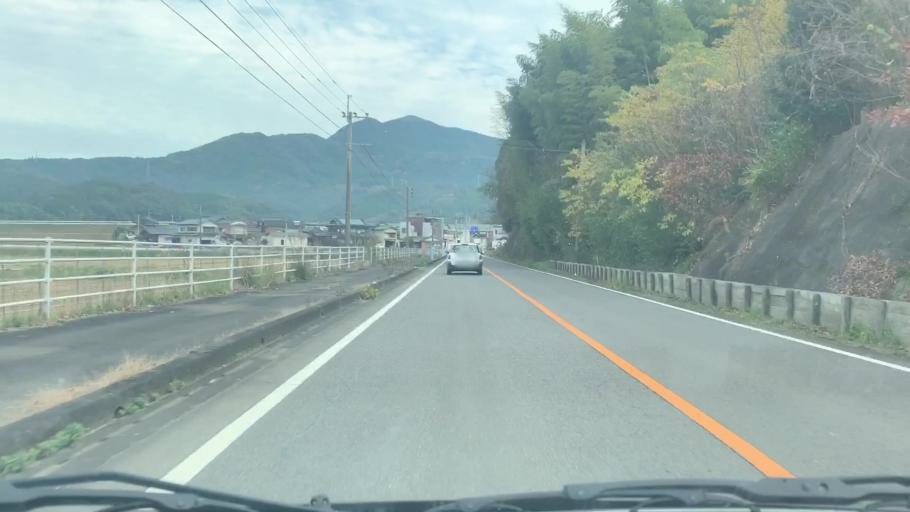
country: JP
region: Saga Prefecture
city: Takeocho-takeo
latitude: 33.2554
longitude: 129.9728
